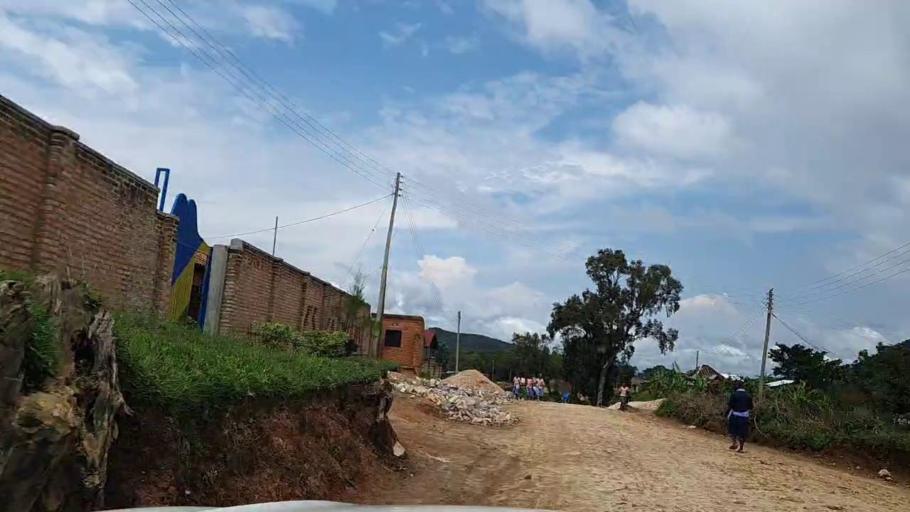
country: RW
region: Southern Province
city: Gikongoro
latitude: -2.3310
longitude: 29.5291
